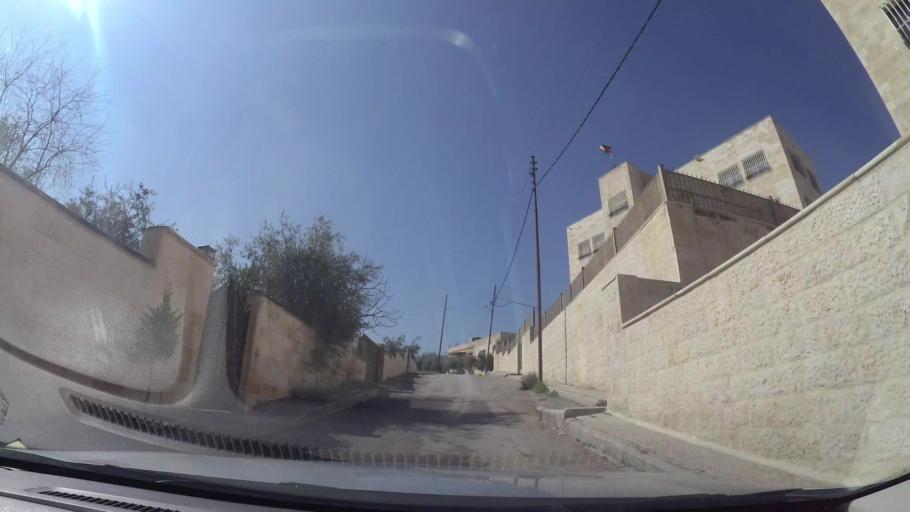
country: JO
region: Amman
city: Al Bunayyat ash Shamaliyah
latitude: 31.8966
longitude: 35.9001
